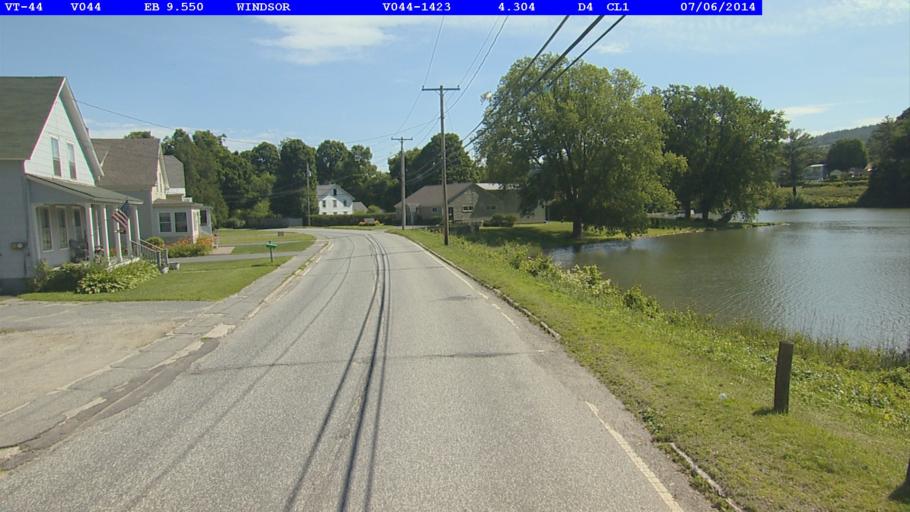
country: US
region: Vermont
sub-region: Windsor County
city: Windsor
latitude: 43.4758
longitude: -72.3982
